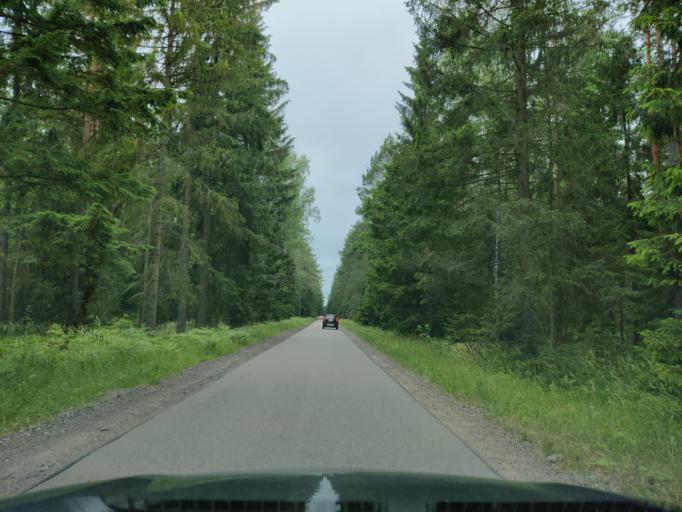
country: PL
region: Warmian-Masurian Voivodeship
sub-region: Powiat szczycienski
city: Rozogi
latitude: 53.5499
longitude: 21.4615
